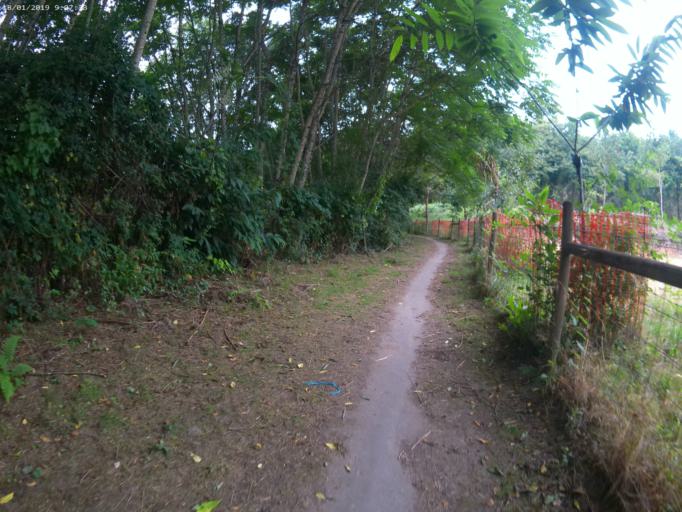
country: PT
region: Viana do Castelo
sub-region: Ponte da Barca
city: Ponte da Barca
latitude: 41.8069
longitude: -8.4472
